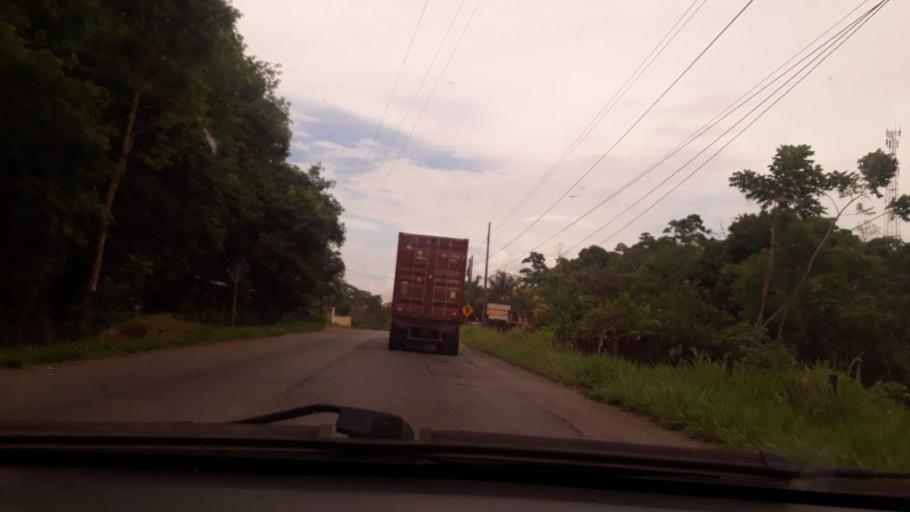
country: GT
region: Izabal
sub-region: Municipio de Puerto Barrios
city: Puerto Barrios
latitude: 15.5745
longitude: -88.6213
